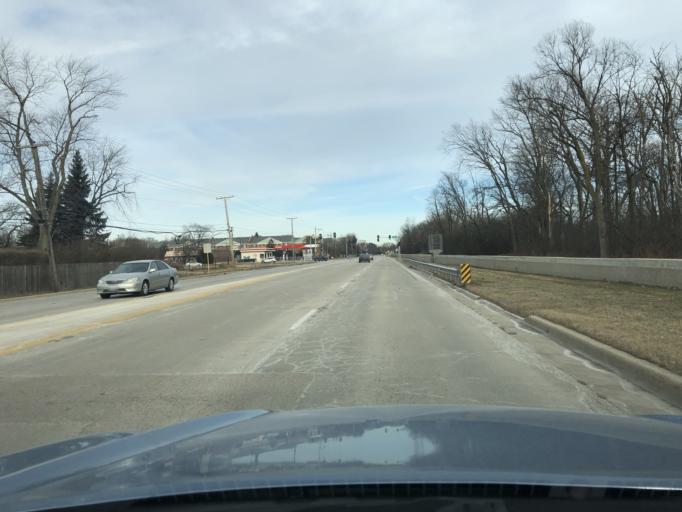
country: US
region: Illinois
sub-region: Cook County
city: Prospect Heights
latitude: 42.0934
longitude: -87.8910
